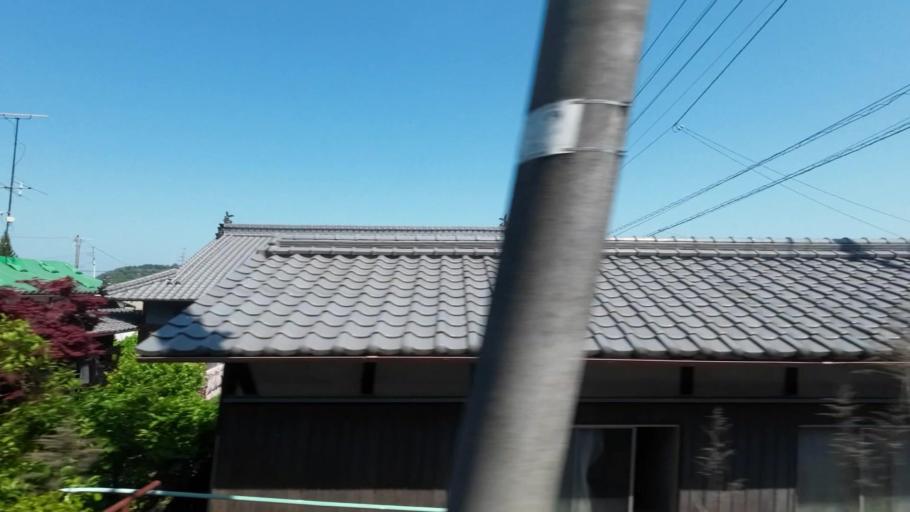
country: JP
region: Ehime
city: Niihama
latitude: 33.9736
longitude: 133.3385
